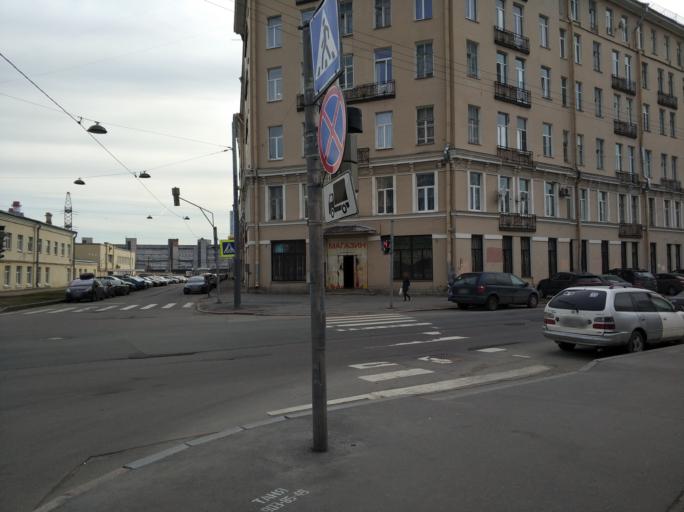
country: RU
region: St.-Petersburg
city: Saint Petersburg
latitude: 59.9046
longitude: 30.3265
